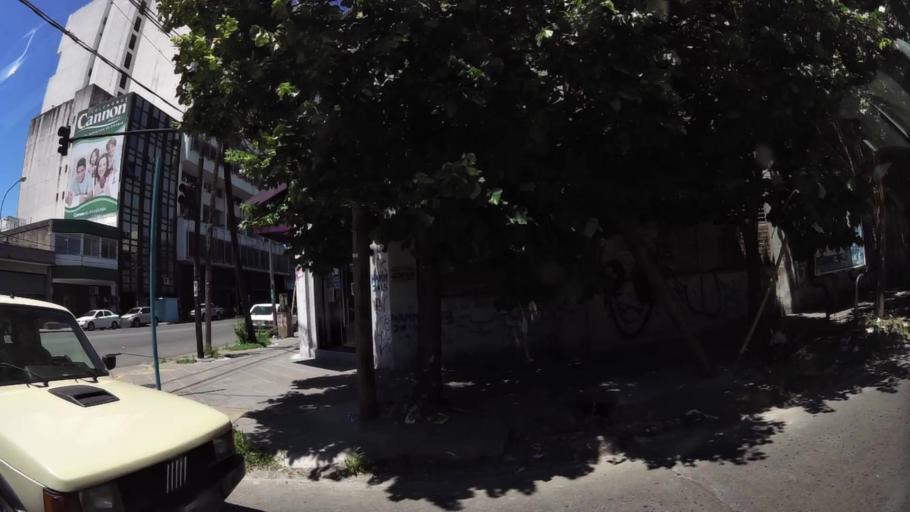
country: AR
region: Buenos Aires
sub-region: Partido de General San Martin
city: General San Martin
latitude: -34.5831
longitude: -58.5396
